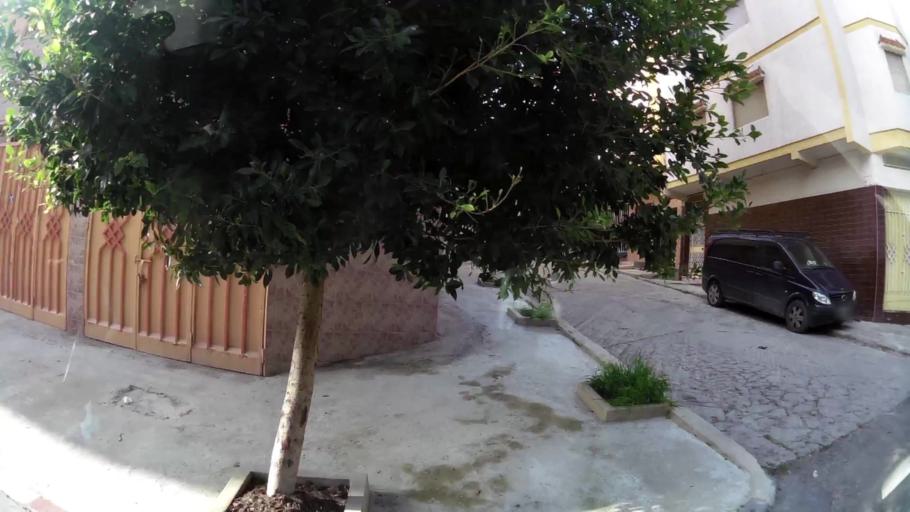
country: MA
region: Tanger-Tetouan
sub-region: Tanger-Assilah
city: Tangier
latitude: 35.7642
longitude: -5.8328
